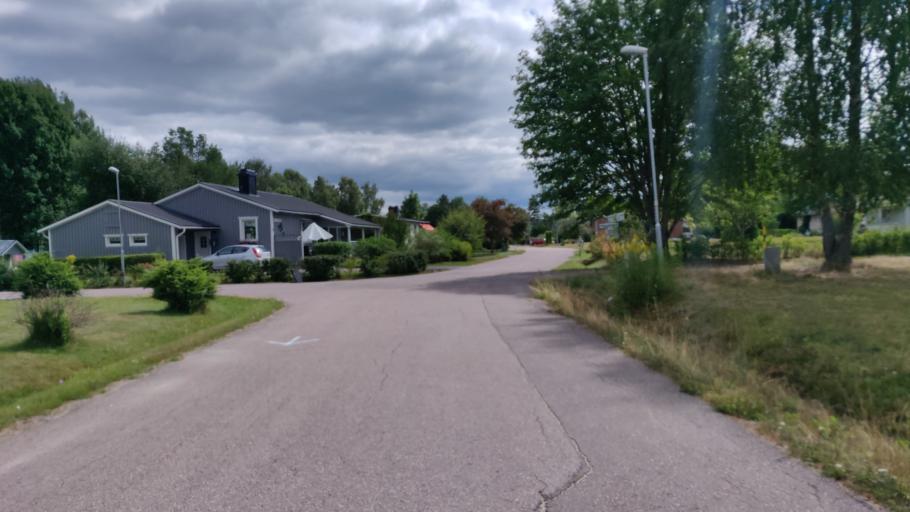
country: SE
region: Vaermland
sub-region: Hagfors Kommun
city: Hagfors
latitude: 60.0056
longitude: 13.5918
